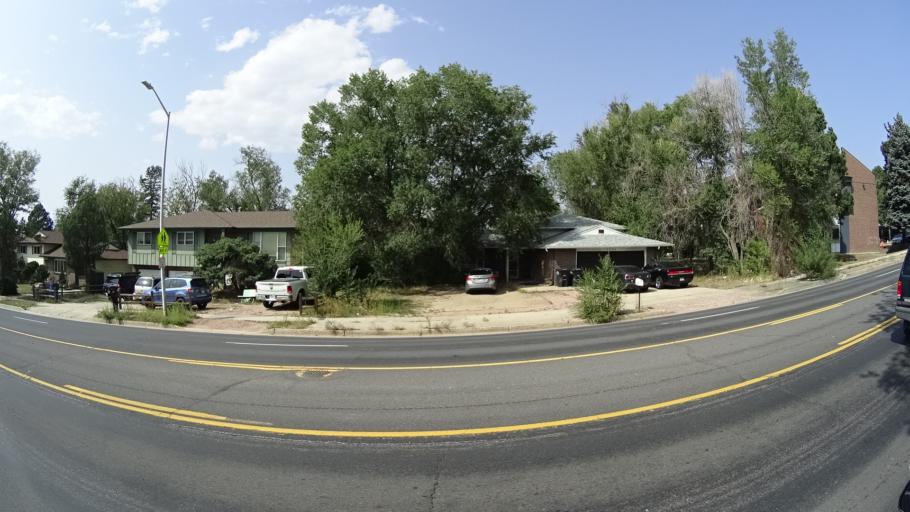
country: US
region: Colorado
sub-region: El Paso County
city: Cimarron Hills
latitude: 38.8558
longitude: -104.7479
